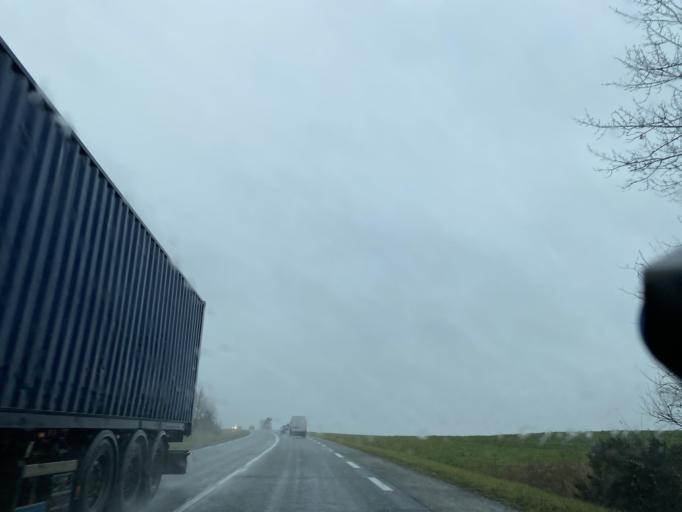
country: FR
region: Centre
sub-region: Departement d'Eure-et-Loir
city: Leves
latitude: 48.4769
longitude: 1.4608
